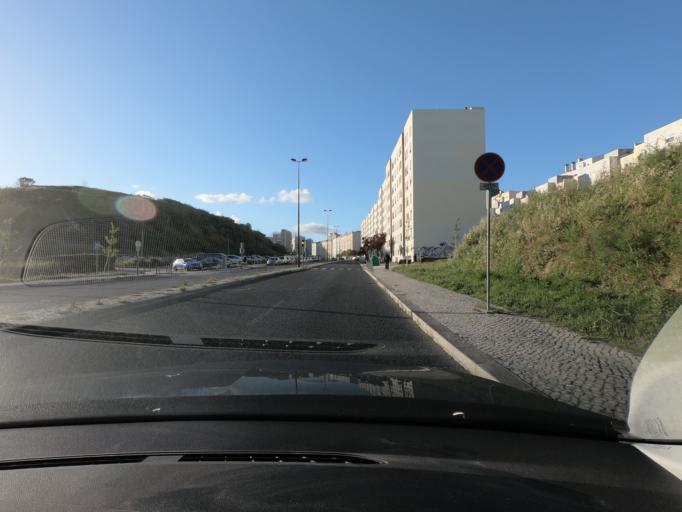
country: PT
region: Lisbon
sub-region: Lisbon
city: Lisbon
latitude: 38.7233
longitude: -9.1216
